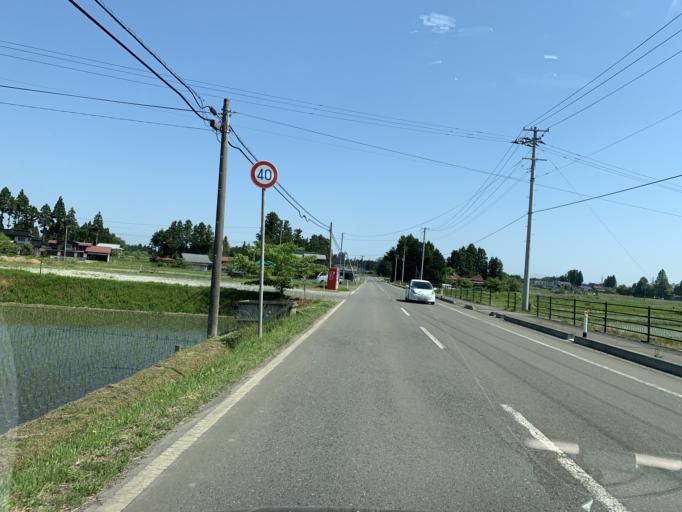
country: JP
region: Iwate
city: Mizusawa
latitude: 39.0933
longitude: 141.0743
